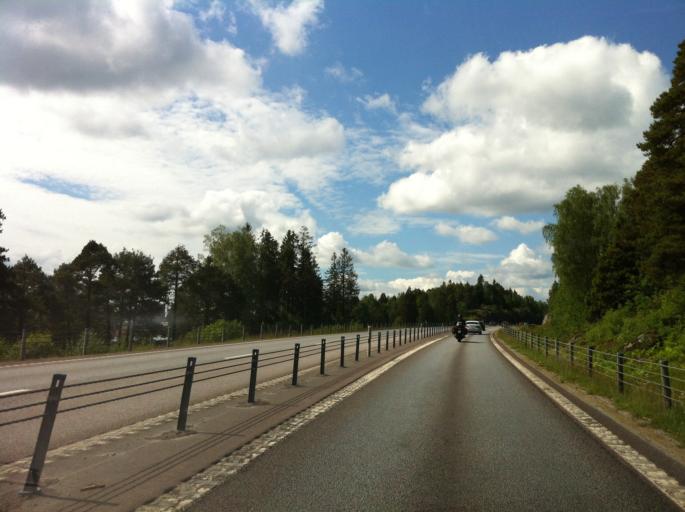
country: SE
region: Vaermland
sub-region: Grums Kommun
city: Grums
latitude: 59.3504
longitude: 13.1264
